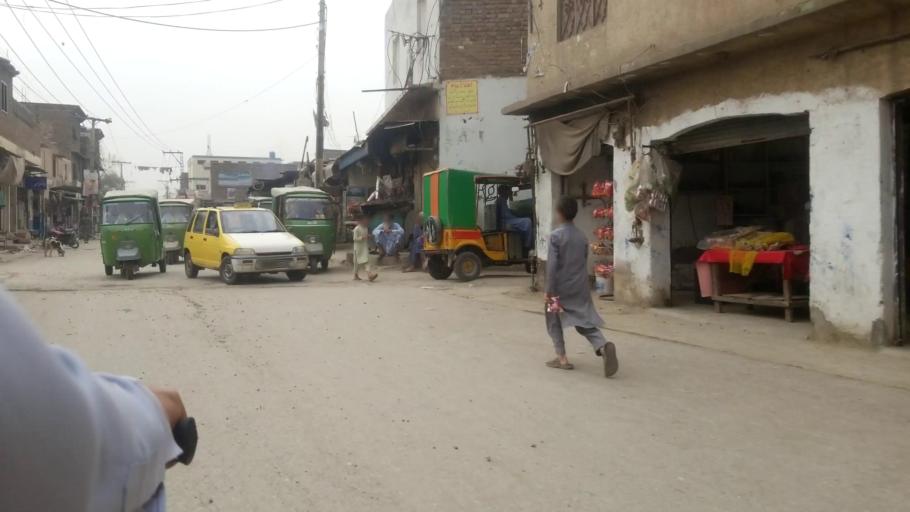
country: PK
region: Khyber Pakhtunkhwa
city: Peshawar
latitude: 33.9898
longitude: 71.5489
